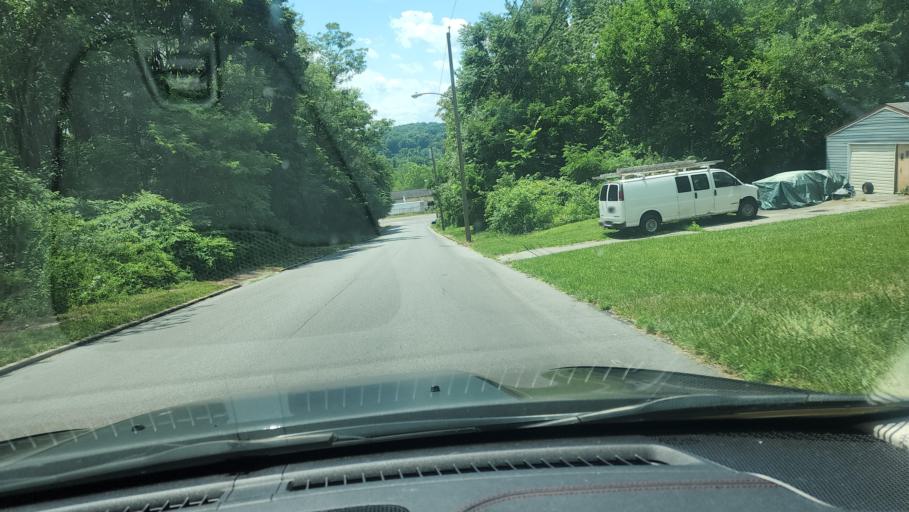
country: US
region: Ohio
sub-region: Mahoning County
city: Campbell
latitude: 41.0738
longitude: -80.5987
